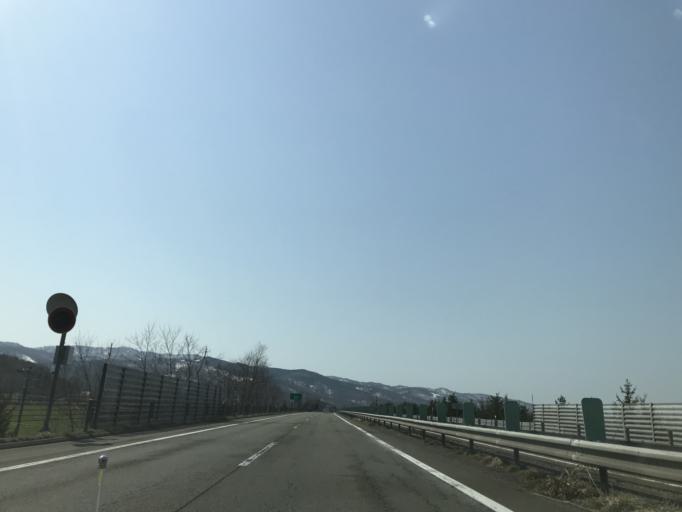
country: JP
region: Hokkaido
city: Bibai
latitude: 43.3457
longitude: 141.8867
